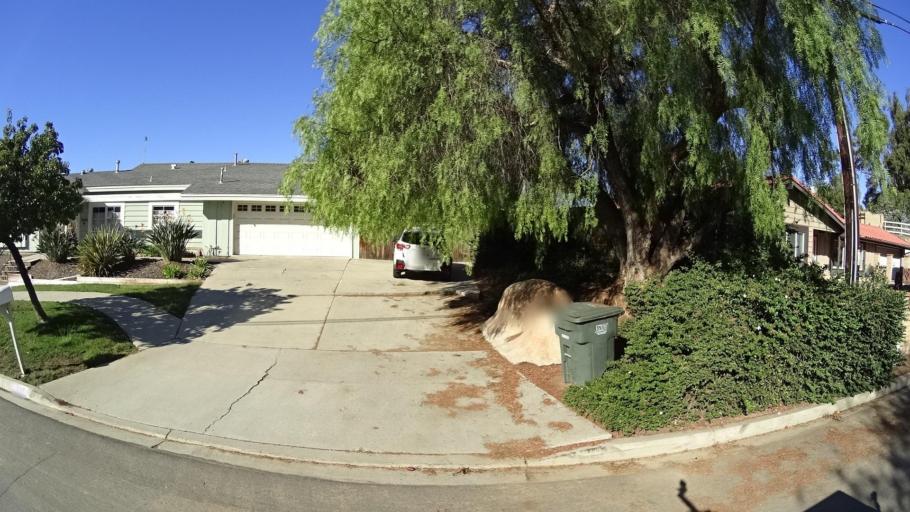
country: US
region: California
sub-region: San Diego County
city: Bonita
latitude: 32.6835
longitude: -117.0167
